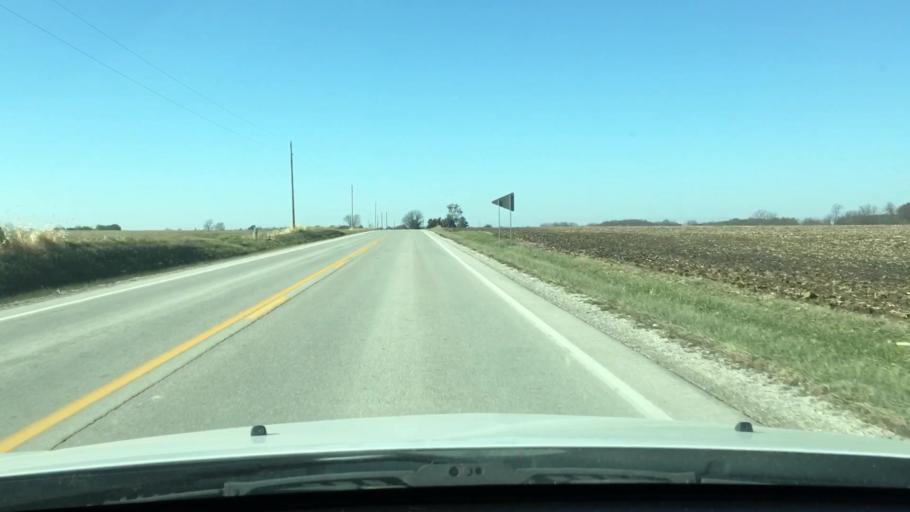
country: US
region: Illinois
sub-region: Pike County
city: Griggsville
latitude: 39.6194
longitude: -90.7153
